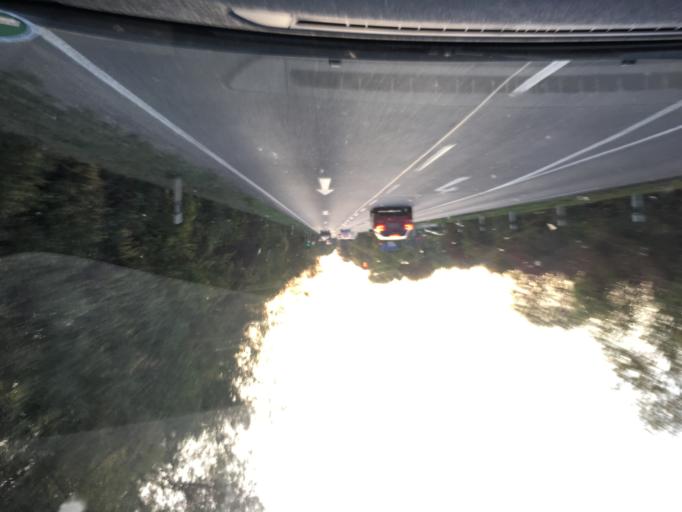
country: DE
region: North Rhine-Westphalia
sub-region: Regierungsbezirk Koln
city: Erftstadt
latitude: 50.8495
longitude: 6.8010
